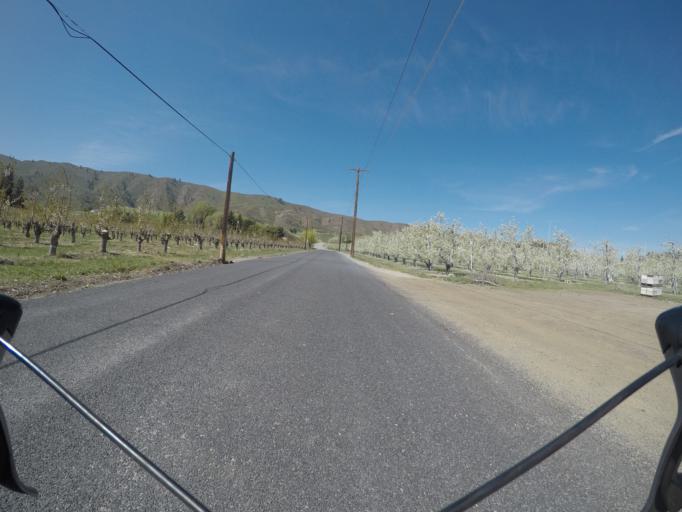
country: US
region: Washington
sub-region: Chelan County
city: Cashmere
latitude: 47.4910
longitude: -120.4299
